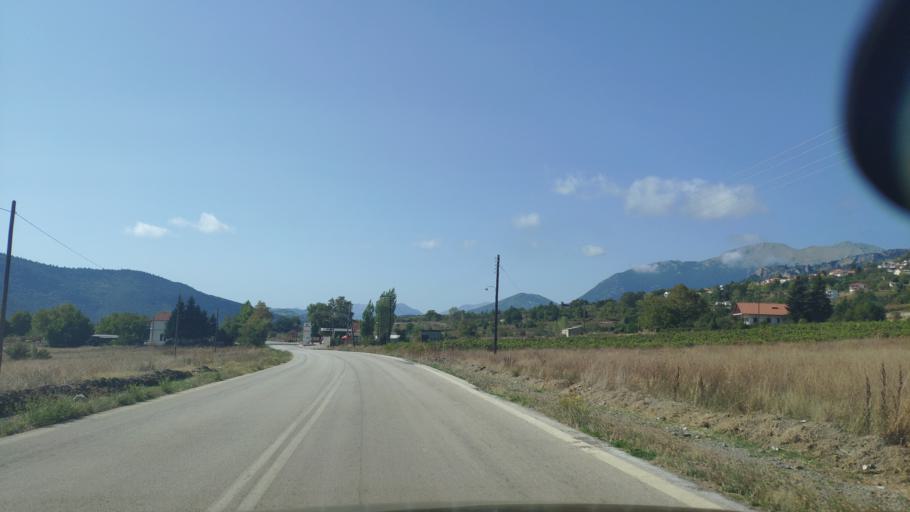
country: GR
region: Peloponnese
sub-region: Nomos Korinthias
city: Xylokastro
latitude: 37.9555
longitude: 22.5760
